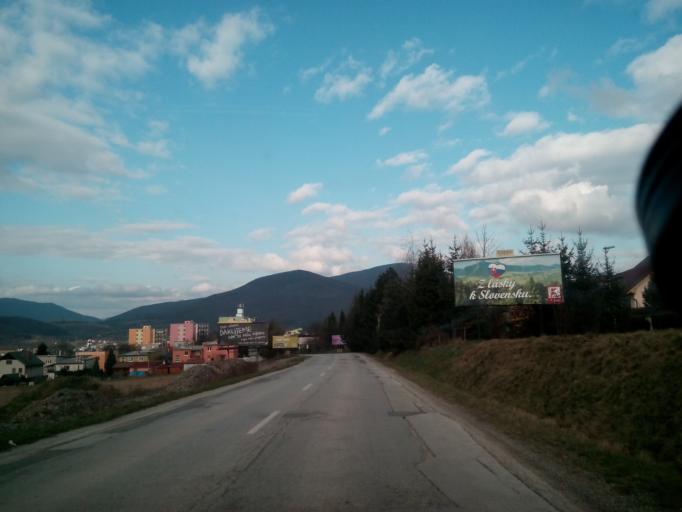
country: SK
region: Kosicky
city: Roznava
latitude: 48.6582
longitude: 20.5467
